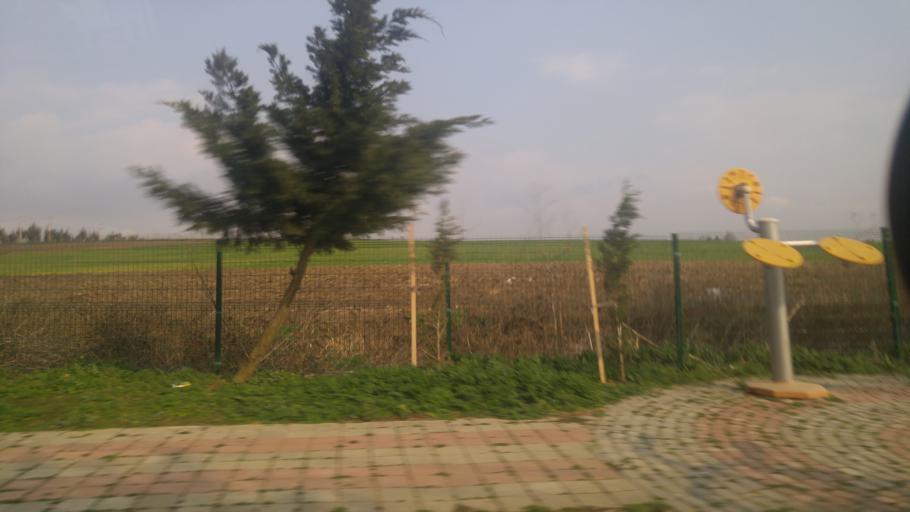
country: TR
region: Istanbul
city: Kavakli
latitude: 41.1291
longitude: 28.3253
